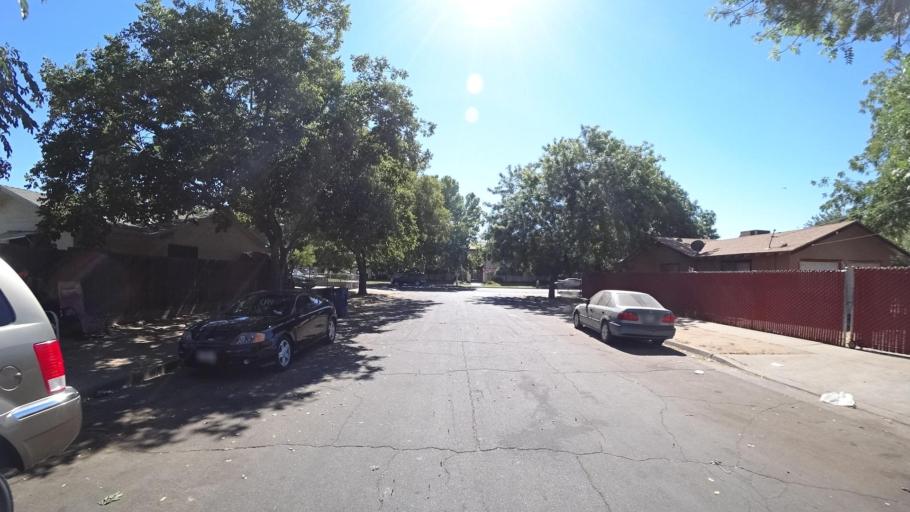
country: US
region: California
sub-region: Fresno County
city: Fresno
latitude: 36.7197
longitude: -119.7924
